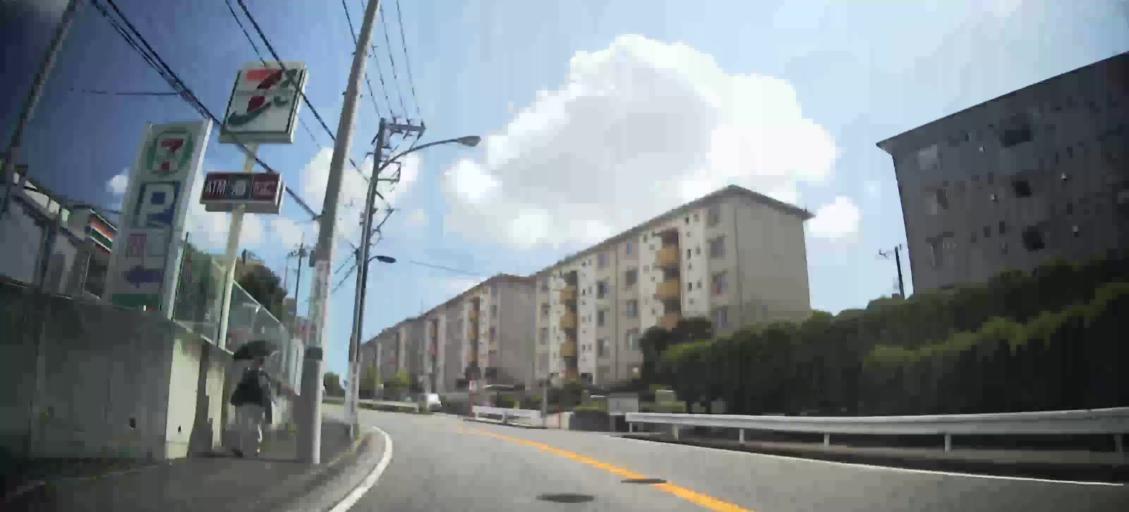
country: JP
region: Kanagawa
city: Yokohama
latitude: 35.4571
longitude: 139.5537
